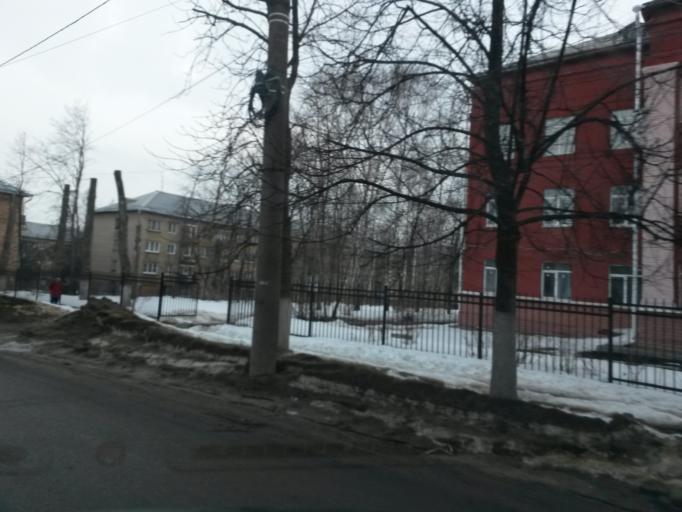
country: RU
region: Jaroslavl
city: Yaroslavl
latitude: 57.5815
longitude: 39.8438
